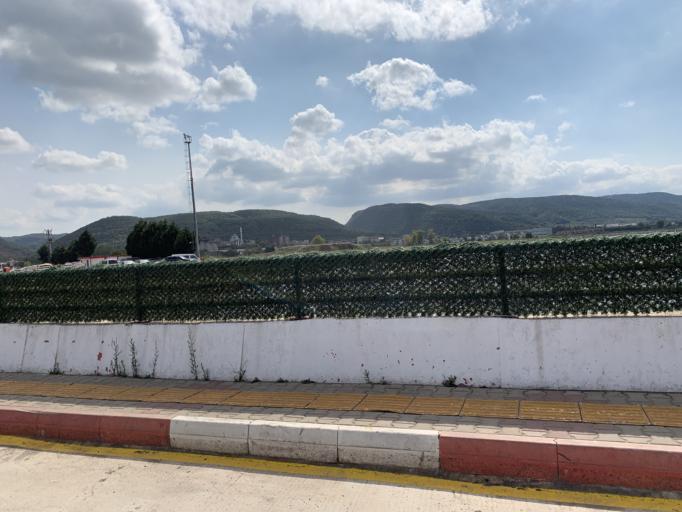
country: TR
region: Yalova
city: Taskopru
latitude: 40.6942
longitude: 29.4462
